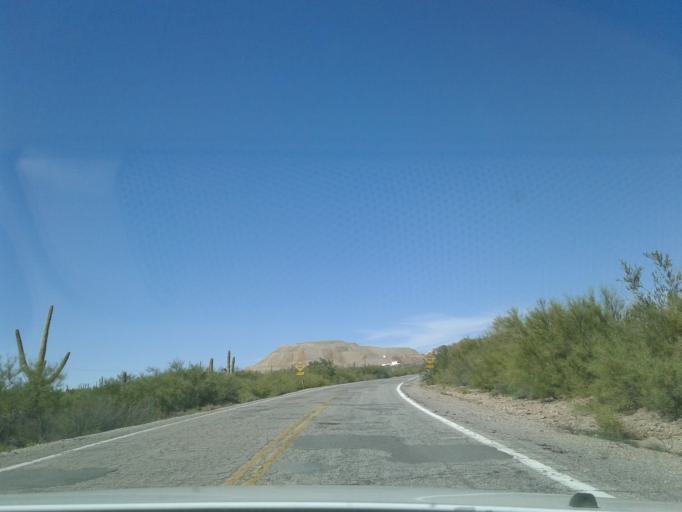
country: US
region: Arizona
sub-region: Pima County
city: Avra Valley
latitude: 32.3794
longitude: -111.4883
